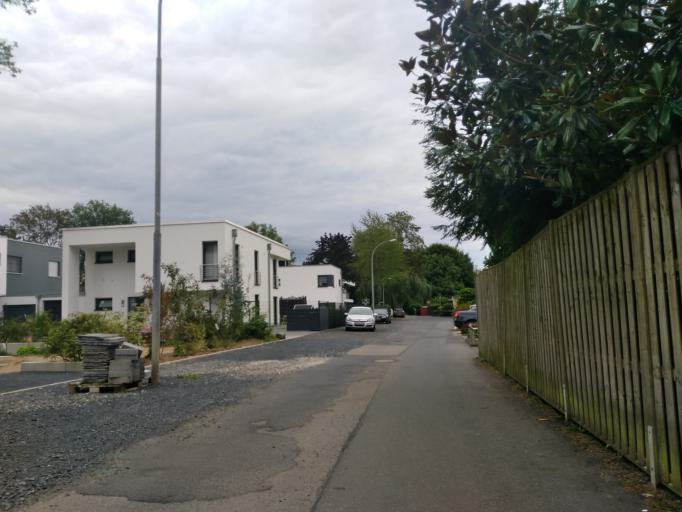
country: DE
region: North Rhine-Westphalia
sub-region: Regierungsbezirk Koln
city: Bad Honnef
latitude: 50.6532
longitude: 7.2144
